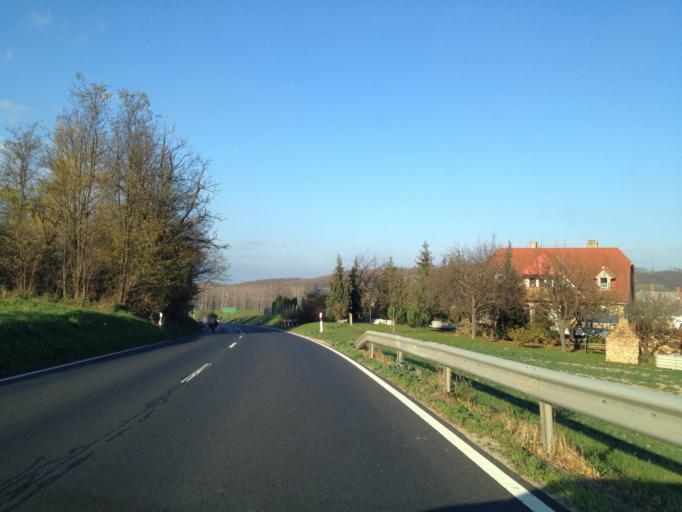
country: HU
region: Gyor-Moson-Sopron
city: Bakonyszentlaszlo
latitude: 47.3636
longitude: 17.8747
